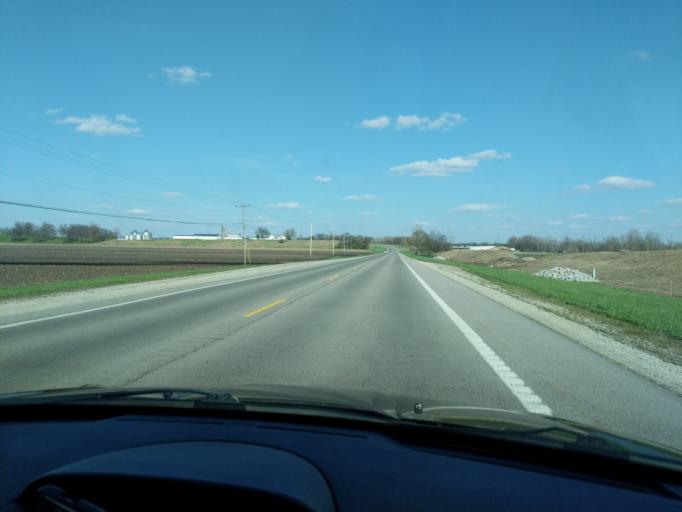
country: US
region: Ohio
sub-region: Champaign County
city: Urbana
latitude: 40.1070
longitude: -83.7909
